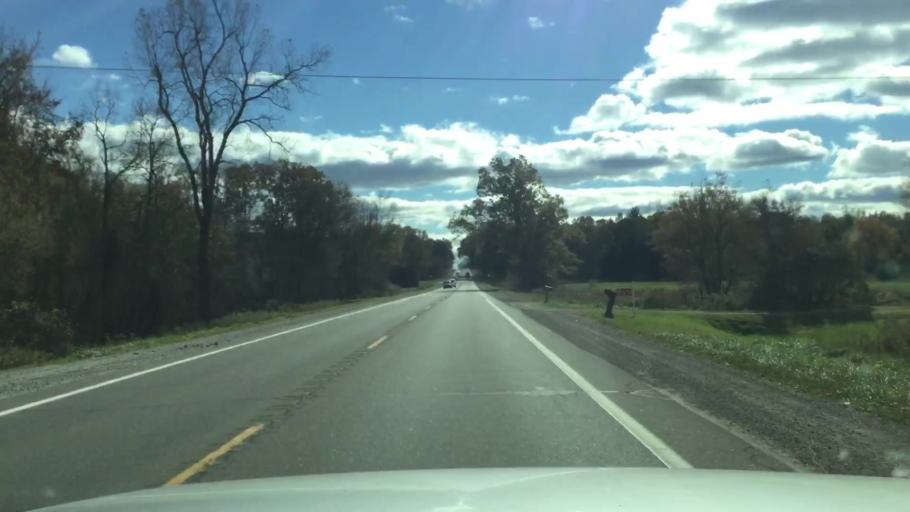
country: US
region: Michigan
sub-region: Lapeer County
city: Barnes Lake-Millers Lake
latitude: 43.1412
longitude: -83.3109
